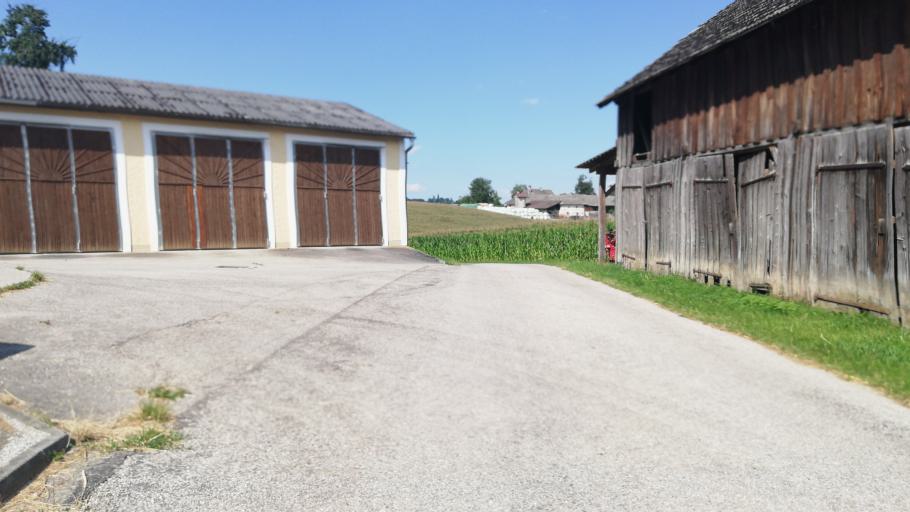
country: AT
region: Upper Austria
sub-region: Wels-Land
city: Edt bei Lambach
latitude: 48.1584
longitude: 13.8987
